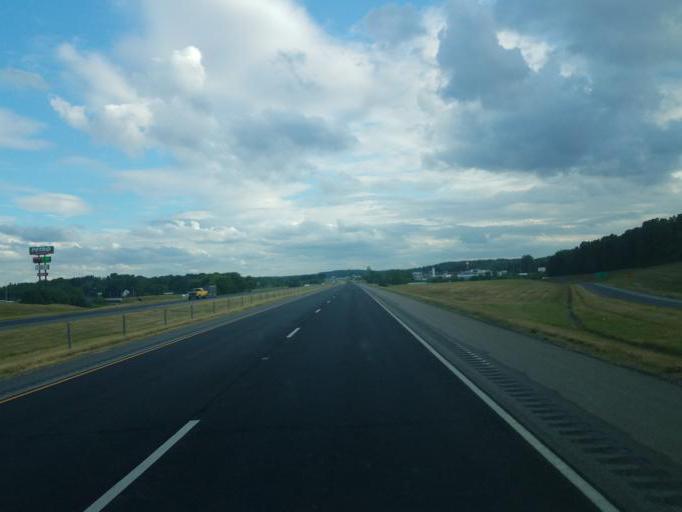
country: US
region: Indiana
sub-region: Steuben County
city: Fremont
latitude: 41.7513
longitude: -84.9943
